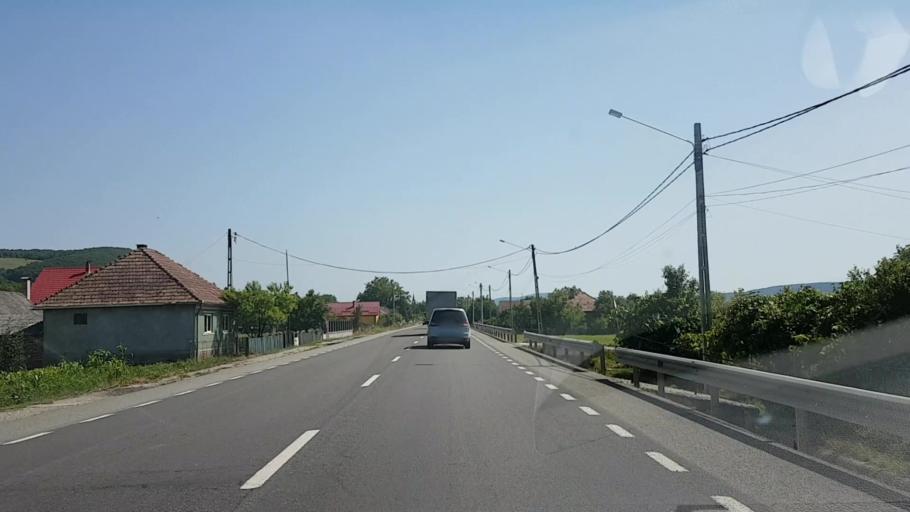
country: RO
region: Bistrita-Nasaud
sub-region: Comuna Sieu-Odorhei
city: Sieu-Odorhei
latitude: 47.1545
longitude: 24.3061
